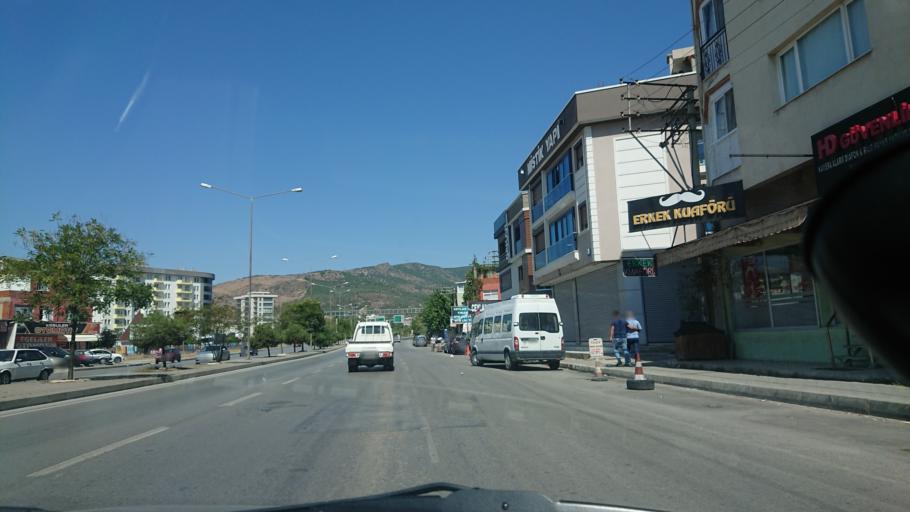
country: TR
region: Izmir
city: Karsiyaka
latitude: 38.4809
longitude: 27.1150
